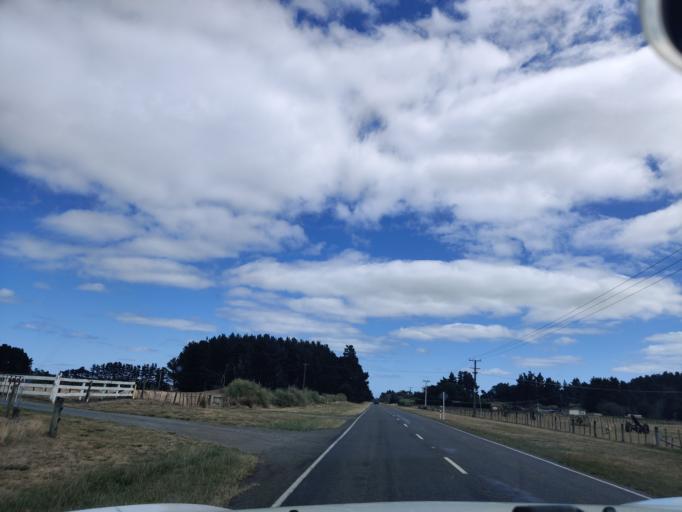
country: NZ
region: Manawatu-Wanganui
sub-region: Horowhenua District
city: Foxton
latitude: -40.3994
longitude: 175.3516
